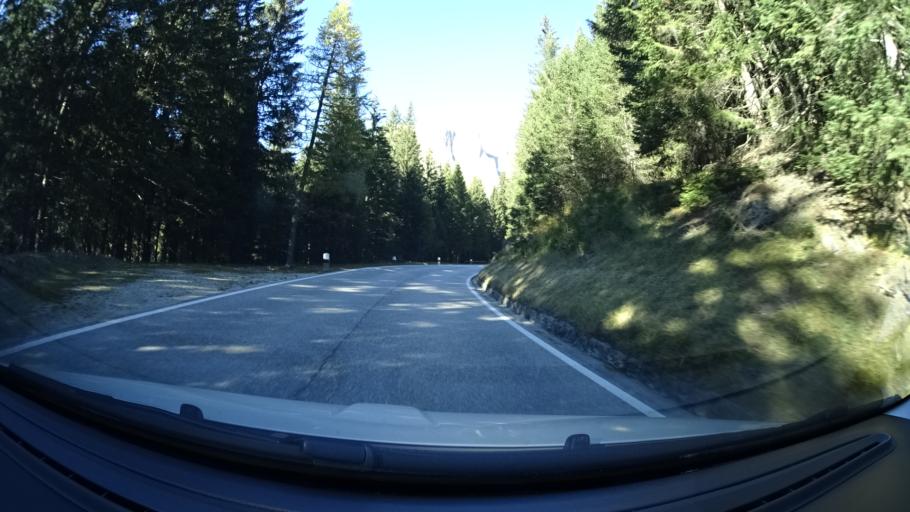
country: IT
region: Trentino-Alto Adige
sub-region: Provincia di Trento
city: Canazei
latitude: 46.4826
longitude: 11.7807
